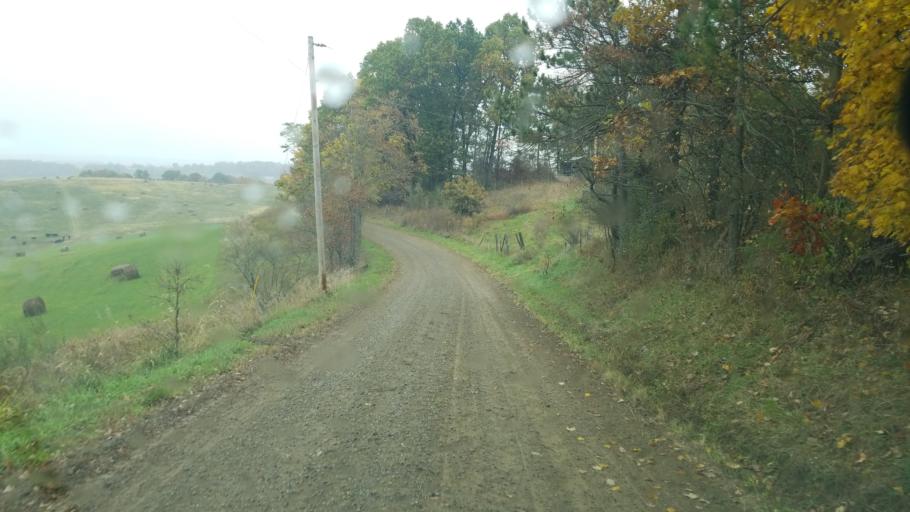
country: US
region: Ohio
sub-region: Coshocton County
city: Coshocton
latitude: 40.4171
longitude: -81.8689
